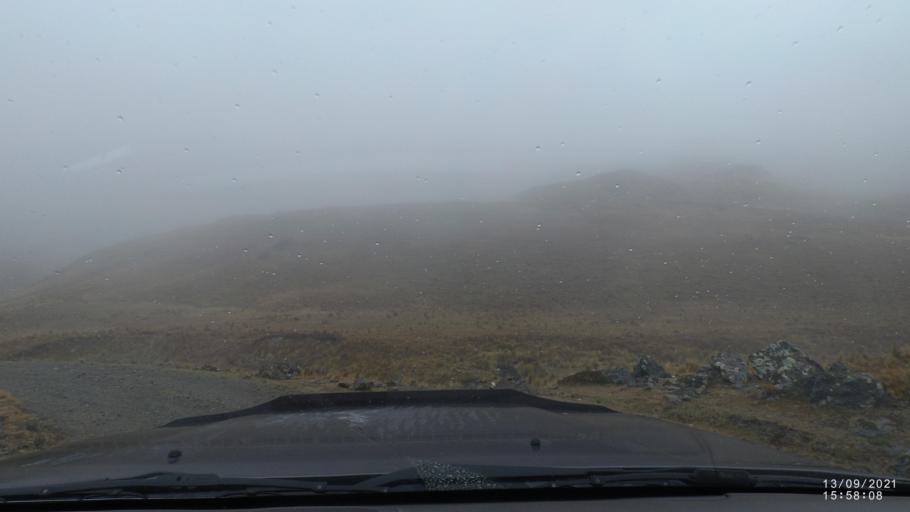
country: BO
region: Cochabamba
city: Colomi
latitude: -17.3013
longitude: -65.7052
